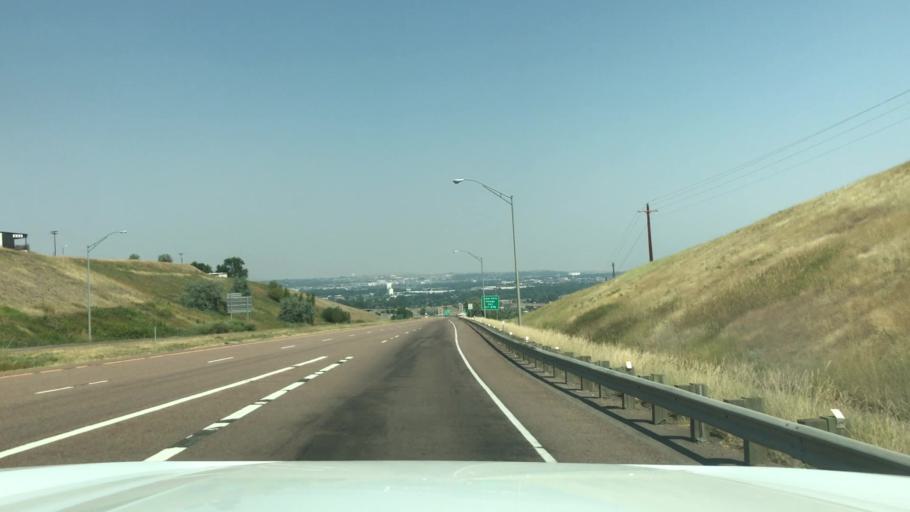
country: US
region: Montana
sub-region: Cascade County
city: Great Falls
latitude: 47.4746
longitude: -111.3573
